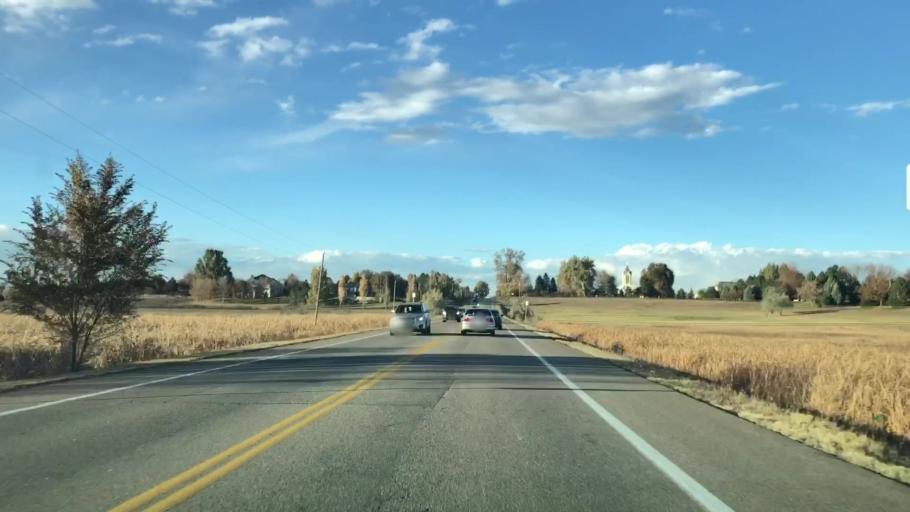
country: US
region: Colorado
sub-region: Larimer County
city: Loveland
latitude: 40.4874
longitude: -105.0393
